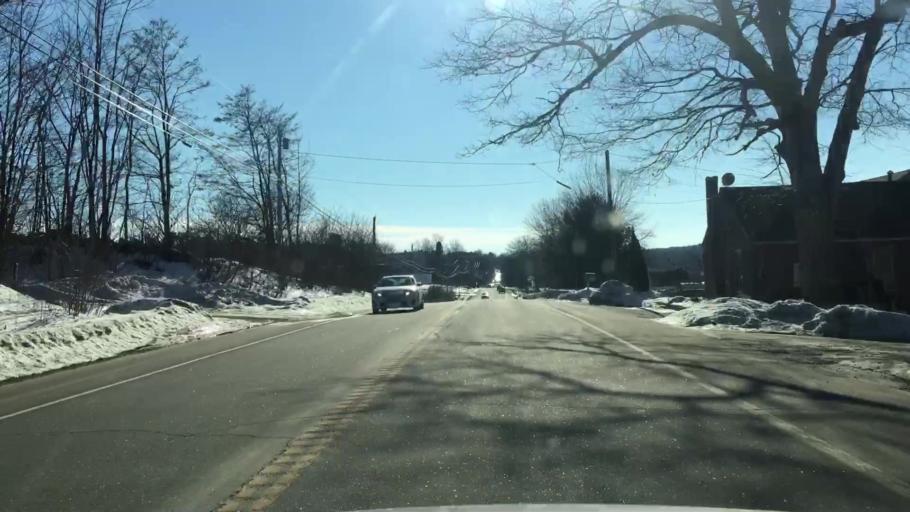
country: US
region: Maine
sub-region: Cumberland County
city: North Windham
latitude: 43.8130
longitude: -70.4002
